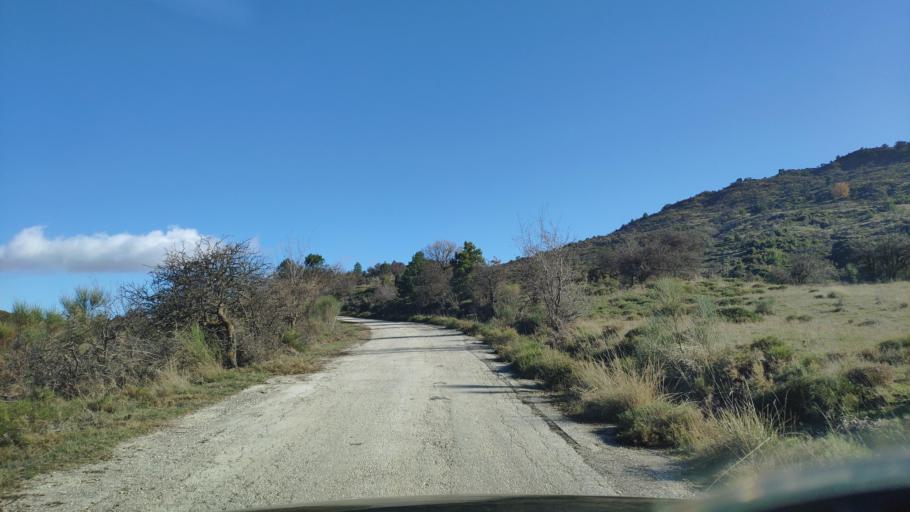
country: GR
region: West Greece
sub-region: Nomos Achaias
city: Aiyira
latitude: 38.0418
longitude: 22.4567
